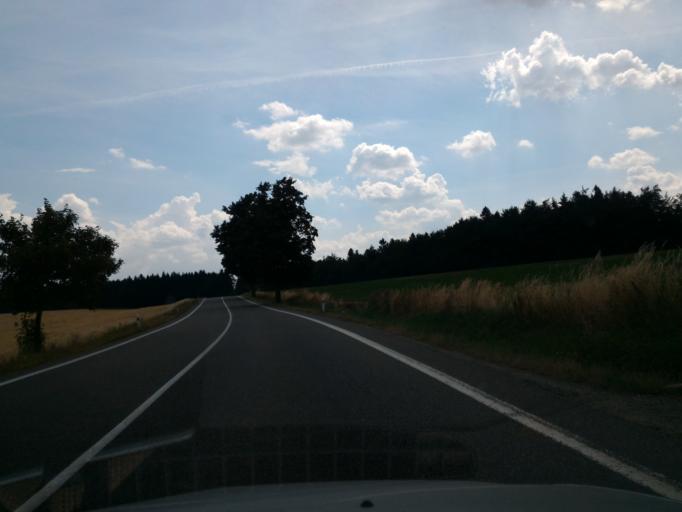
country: CZ
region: Vysocina
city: Bohdalov
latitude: 49.4700
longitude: 15.8254
